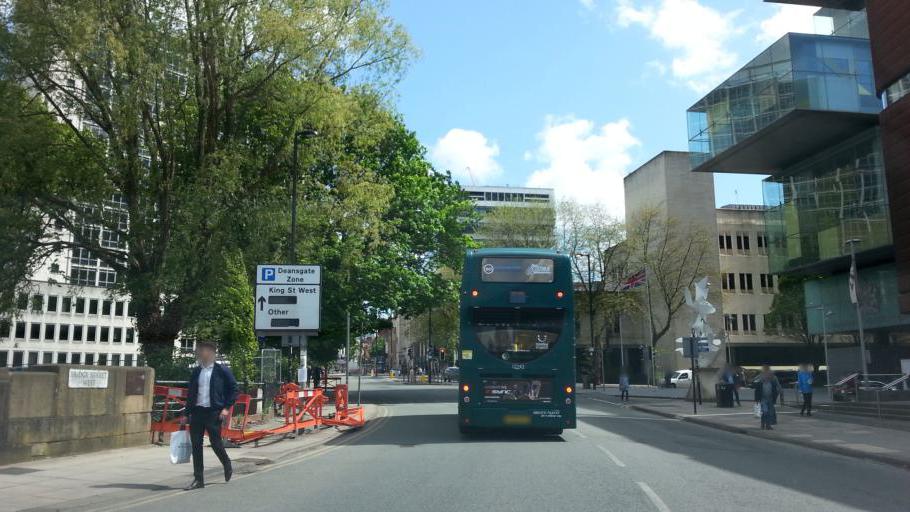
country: GB
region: England
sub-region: Manchester
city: Manchester
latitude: 53.4813
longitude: -2.2532
